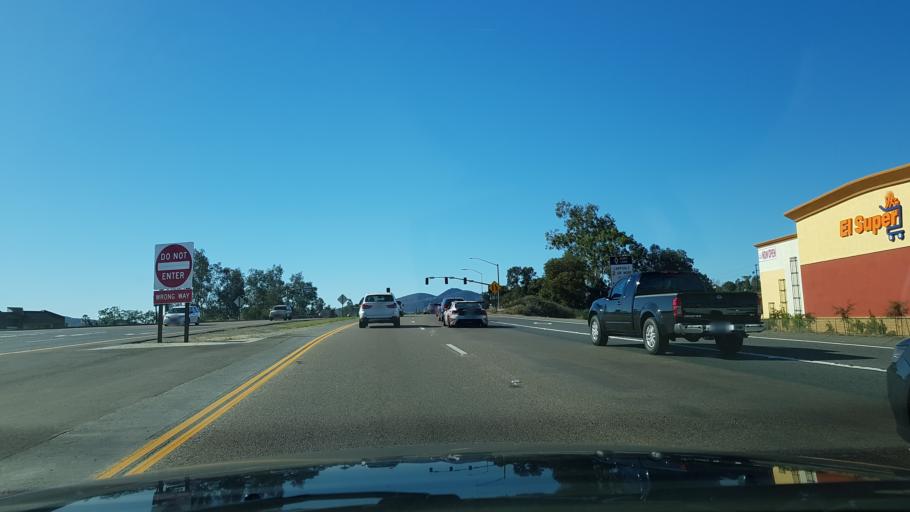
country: US
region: California
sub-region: San Diego County
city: Escondido
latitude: 33.1326
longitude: -117.0876
